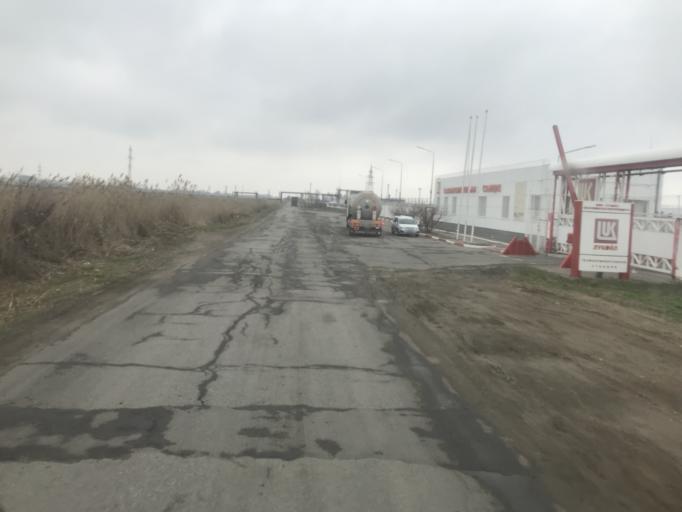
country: RU
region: Volgograd
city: Svetlyy Yar
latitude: 48.5118
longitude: 44.6369
